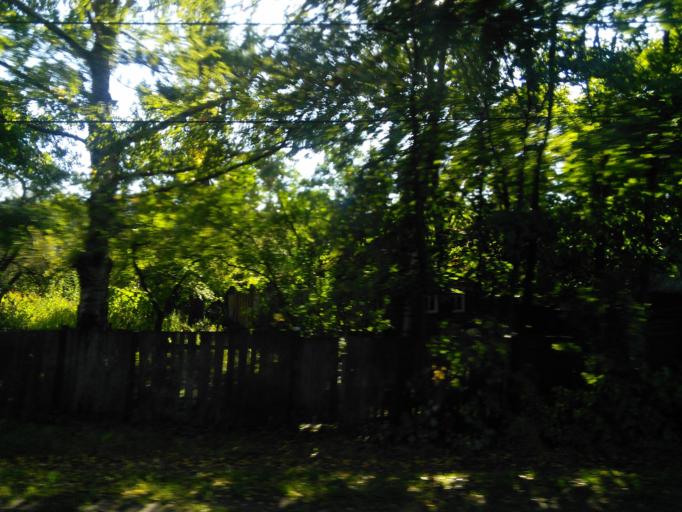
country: RU
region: Jaroslavl
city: Rybinsk
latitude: 58.0580
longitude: 38.8543
